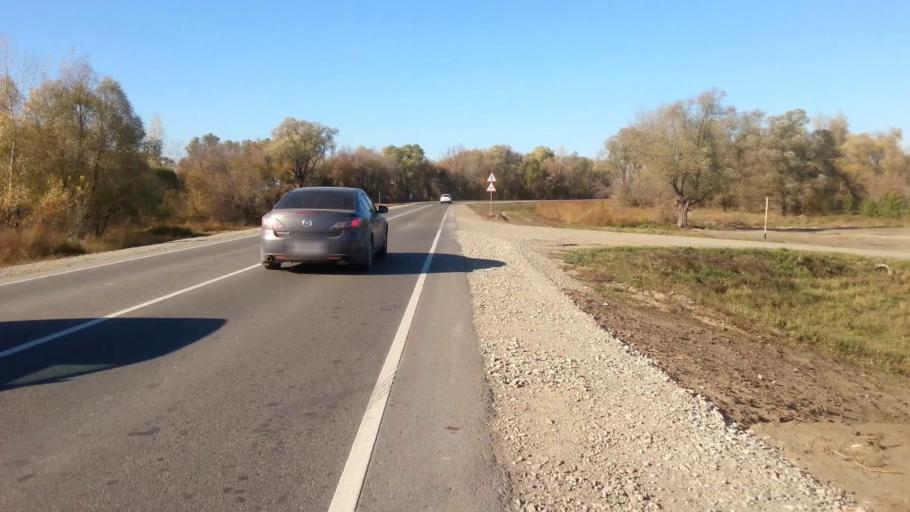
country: RU
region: Altai Krai
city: Sannikovo
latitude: 53.3206
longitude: 83.9436
